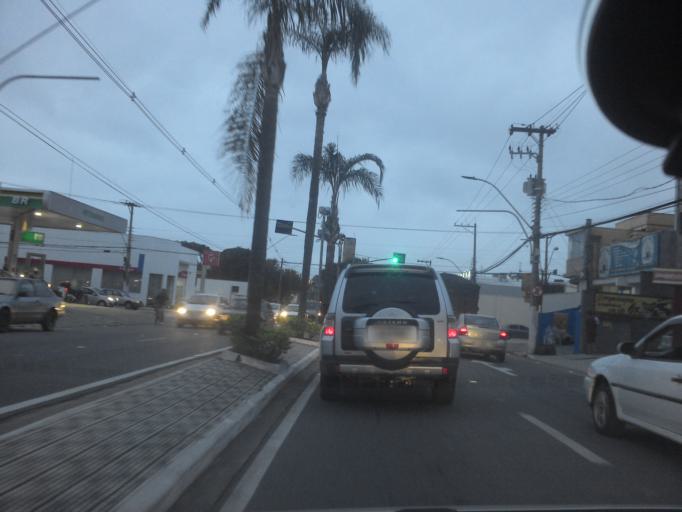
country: BR
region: Sao Paulo
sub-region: Taubate
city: Taubate
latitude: -23.0213
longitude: -45.5383
